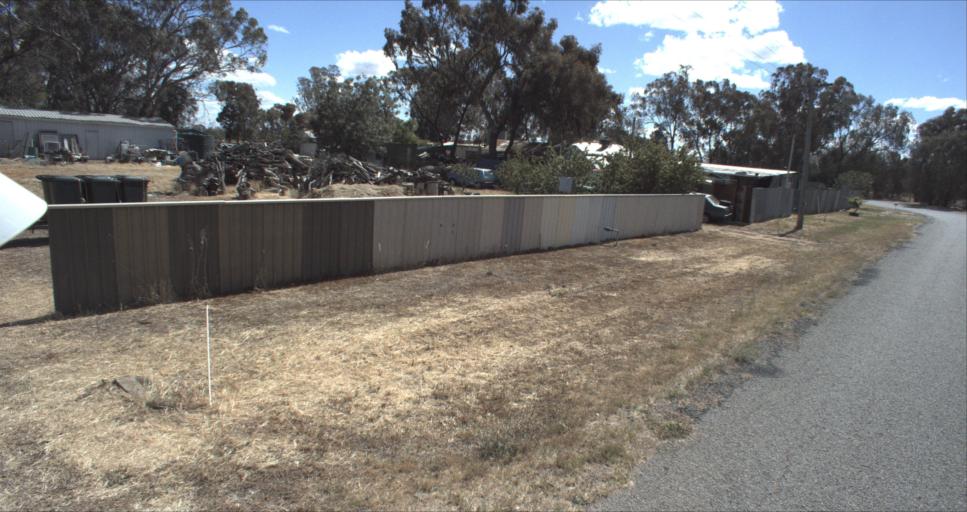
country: AU
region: New South Wales
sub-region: Leeton
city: Leeton
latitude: -34.5168
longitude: 146.2343
